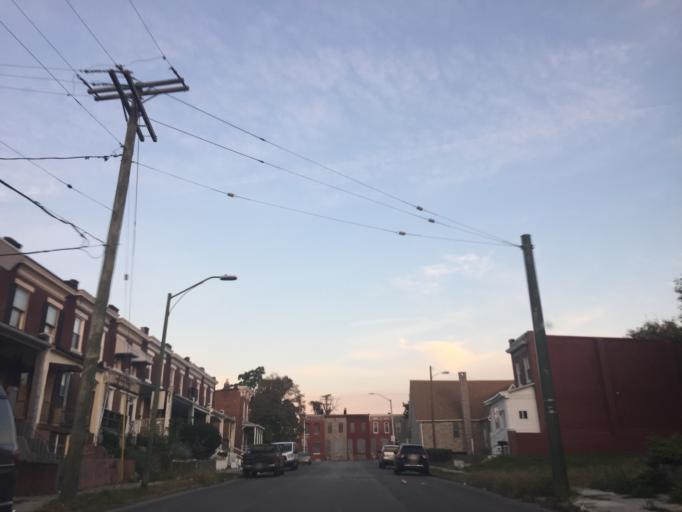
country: US
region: Maryland
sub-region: City of Baltimore
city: Baltimore
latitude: 39.3162
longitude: -76.6077
